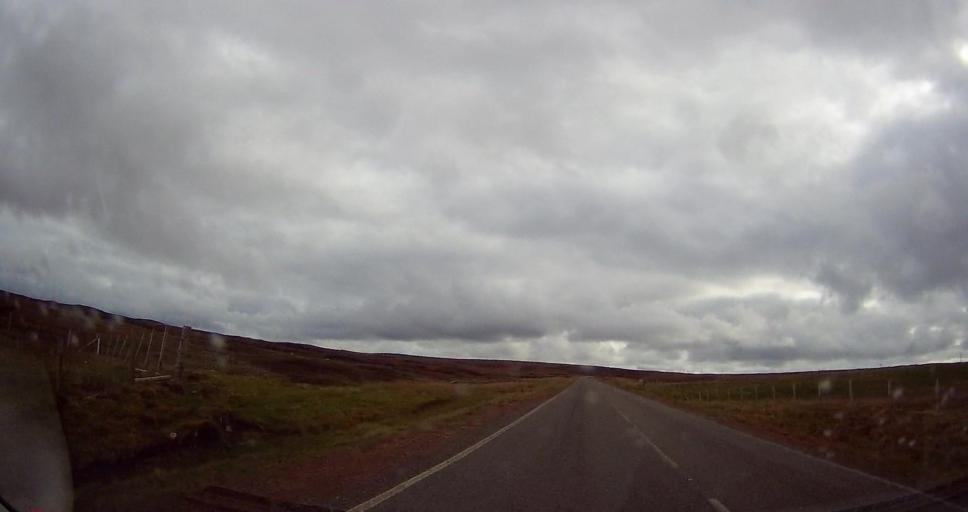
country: GB
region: Scotland
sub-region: Shetland Islands
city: Shetland
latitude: 60.6624
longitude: -1.0431
